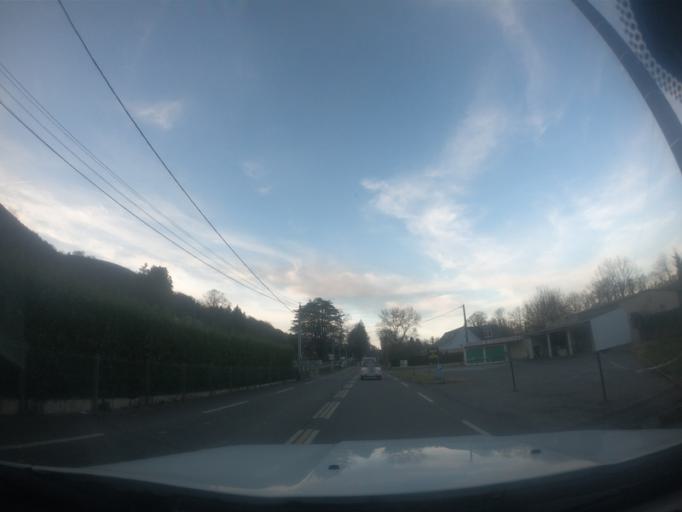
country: FR
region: Midi-Pyrenees
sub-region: Departement des Hautes-Pyrenees
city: Gerde
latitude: 43.0407
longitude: 0.1611
